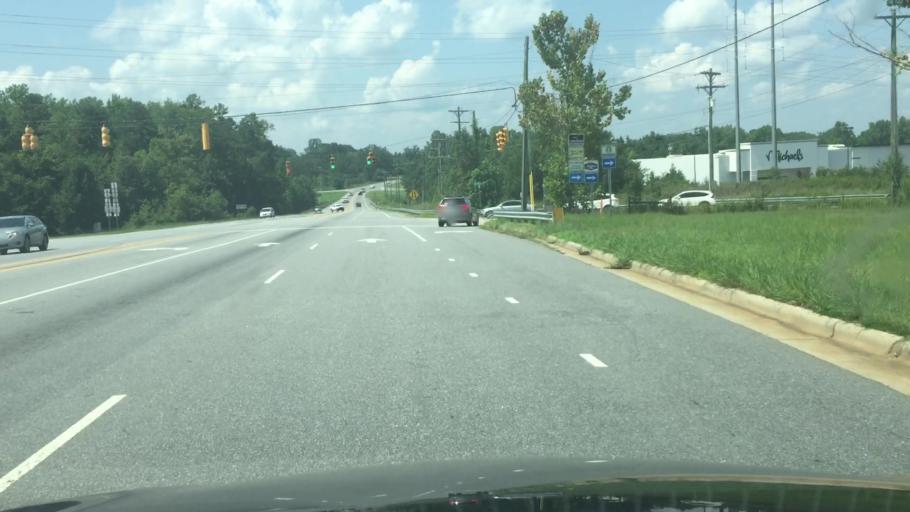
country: US
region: North Carolina
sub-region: Rowan County
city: Salisbury
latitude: 35.6354
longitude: -80.4904
